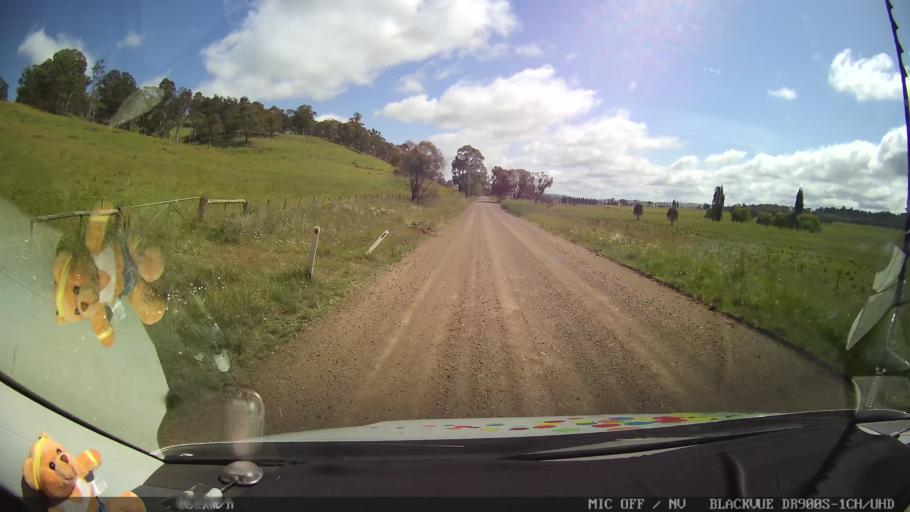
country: AU
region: New South Wales
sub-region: Glen Innes Severn
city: Glen Innes
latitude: -29.9567
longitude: 151.7029
